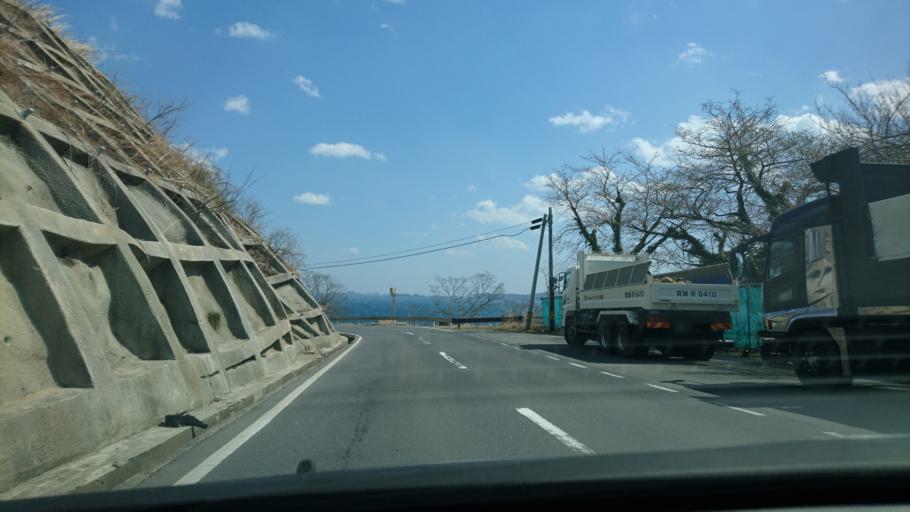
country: JP
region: Miyagi
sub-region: Oshika Gun
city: Onagawa Cho
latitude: 38.4397
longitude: 141.4686
